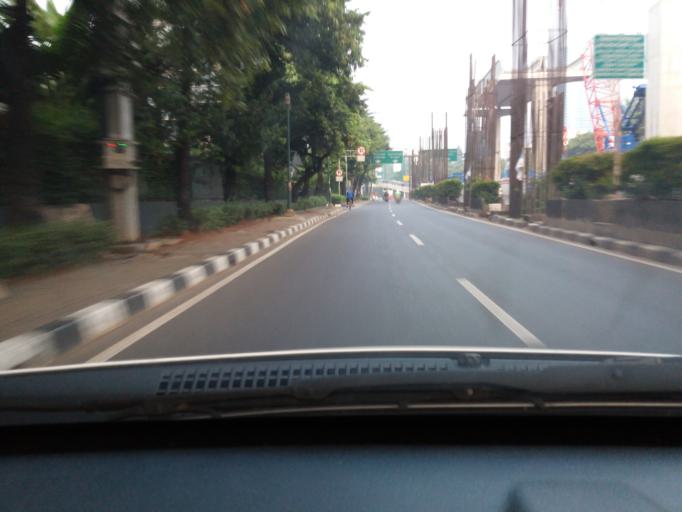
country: ID
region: Jakarta Raya
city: Jakarta
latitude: -6.2343
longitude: 106.8304
